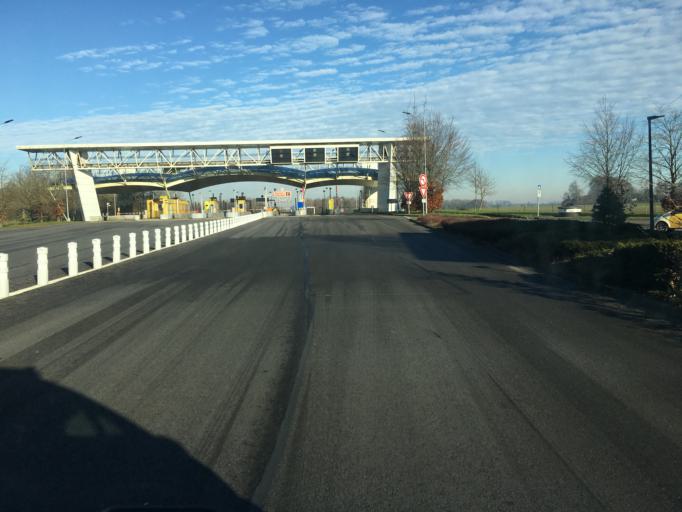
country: FR
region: Haute-Normandie
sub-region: Departement de la Seine-Maritime
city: Yerville
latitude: 49.6469
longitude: 0.8422
